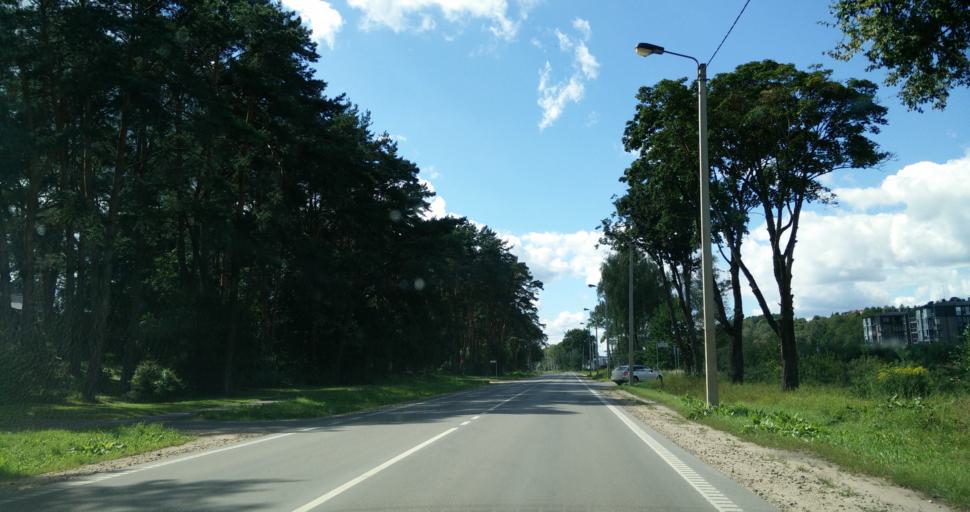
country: LT
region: Kauno apskritis
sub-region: Kauno rajonas
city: Akademija (Kaunas)
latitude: 54.9207
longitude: 23.8146
